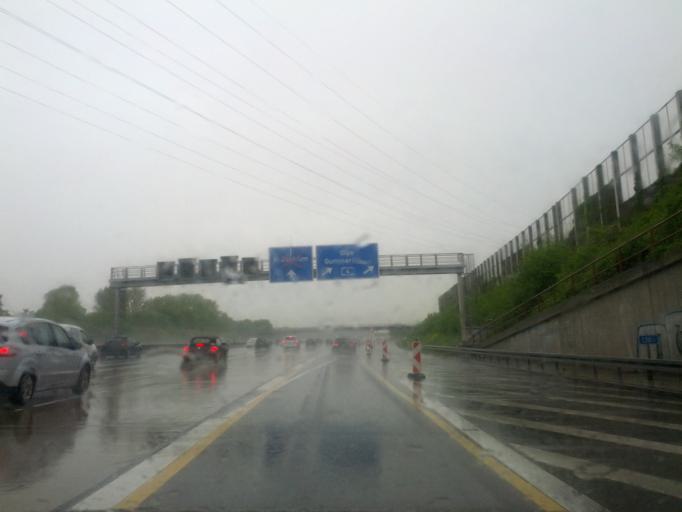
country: DE
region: North Rhine-Westphalia
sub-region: Regierungsbezirk Koln
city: Merheim
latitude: 50.9454
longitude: 7.0398
